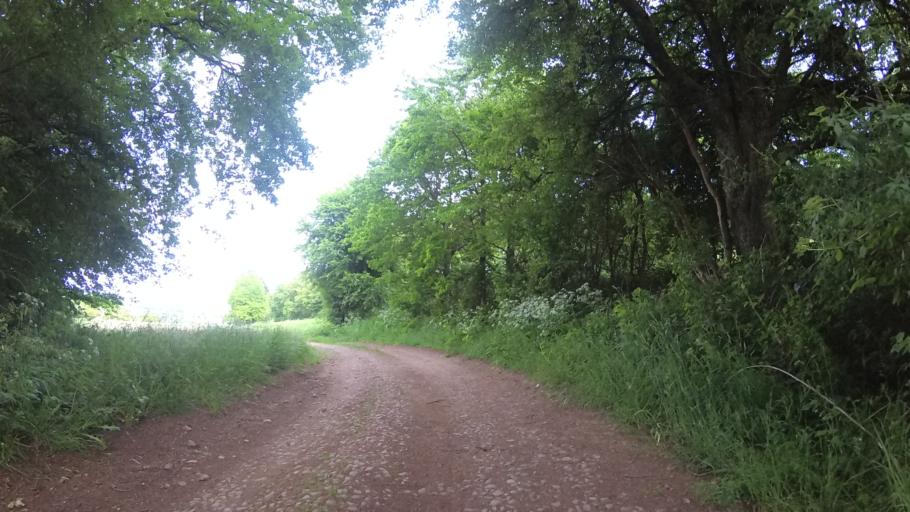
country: DE
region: Saarland
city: Hangard
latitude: 49.4263
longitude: 7.2056
